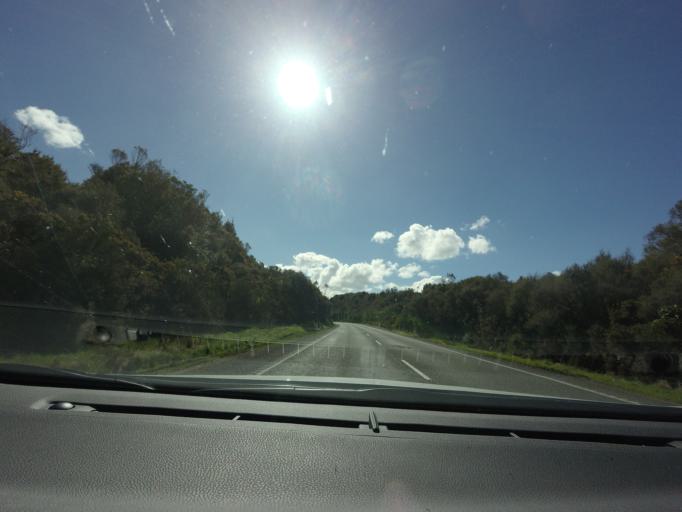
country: NZ
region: Bay of Plenty
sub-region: Rotorua District
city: Rotorua
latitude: -38.0388
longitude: 176.0525
